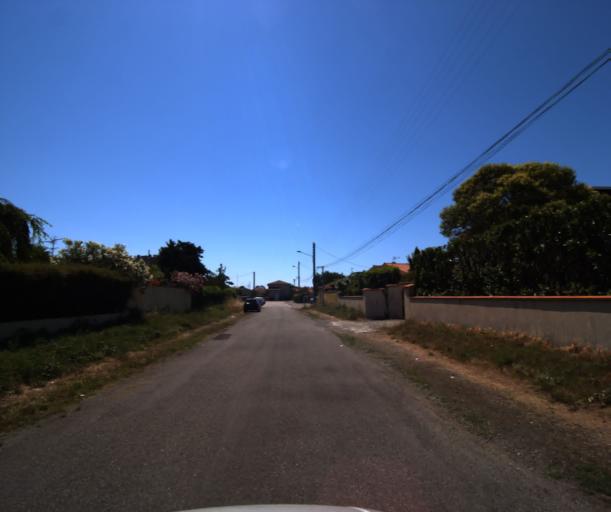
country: FR
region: Midi-Pyrenees
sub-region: Departement de la Haute-Garonne
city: Seysses
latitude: 43.4655
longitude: 1.3157
